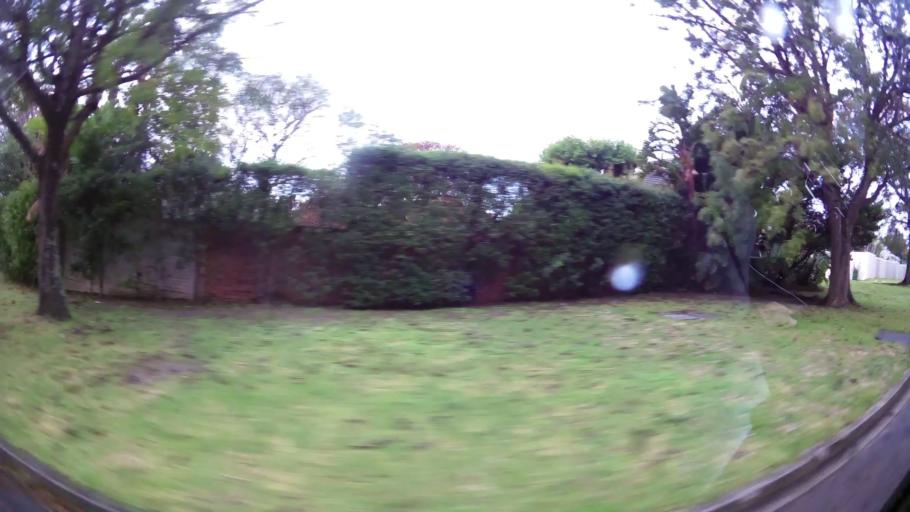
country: ZA
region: Eastern Cape
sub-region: Nelson Mandela Bay Metropolitan Municipality
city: Port Elizabeth
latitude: -33.9752
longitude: 25.5660
